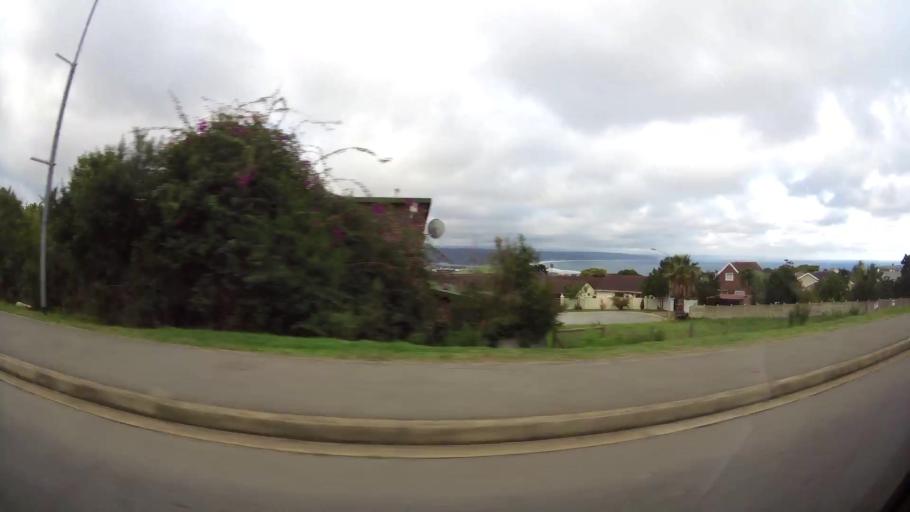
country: ZA
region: Western Cape
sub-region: Eden District Municipality
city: Plettenberg Bay
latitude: -34.0523
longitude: 23.3629
